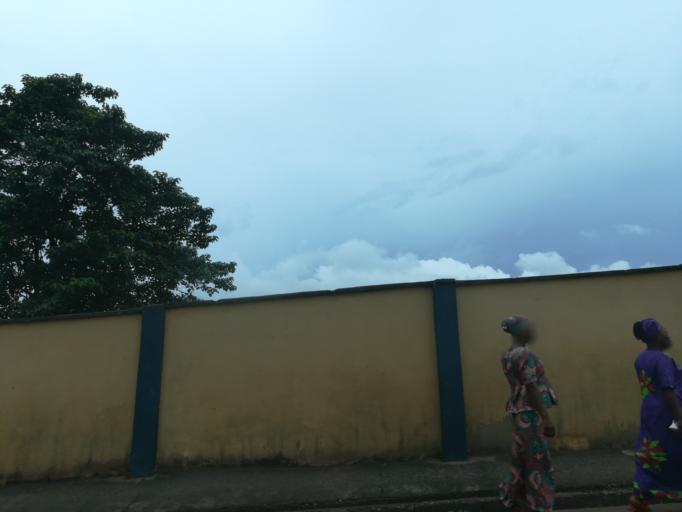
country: NG
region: Lagos
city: Agege
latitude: 6.6150
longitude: 3.3187
